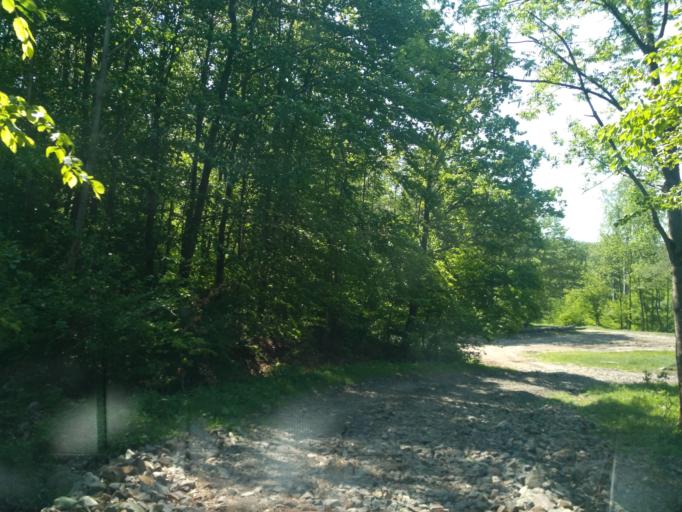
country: SK
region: Presovsky
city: Vranov nad Topl'ou
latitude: 48.8406
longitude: 21.4782
